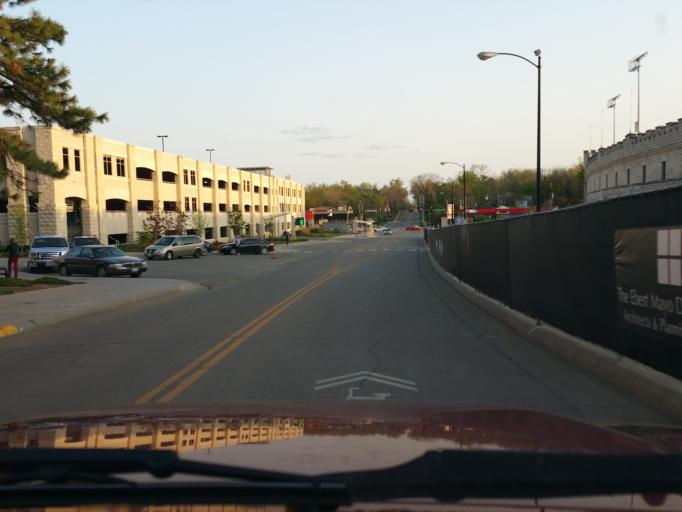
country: US
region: Kansas
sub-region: Riley County
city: Manhattan
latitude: 39.1881
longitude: -96.5832
